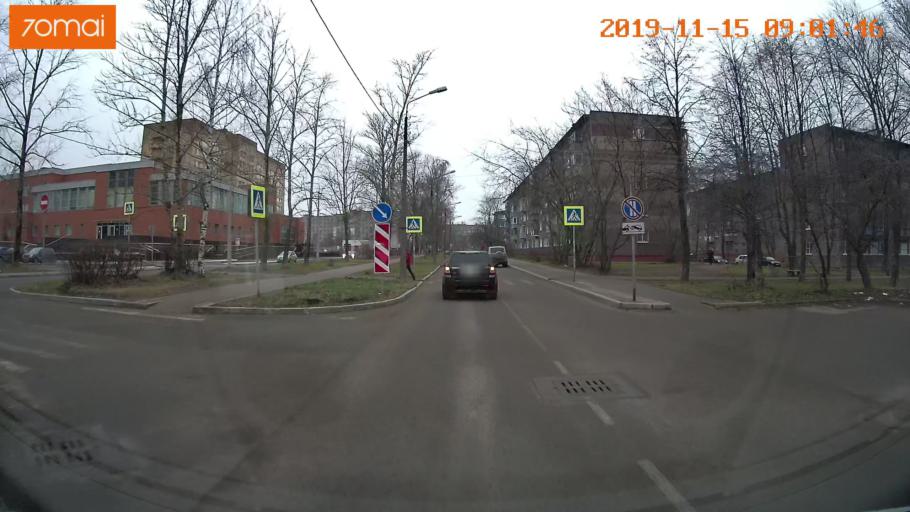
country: RU
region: Vologda
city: Cherepovets
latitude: 59.1341
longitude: 37.9267
